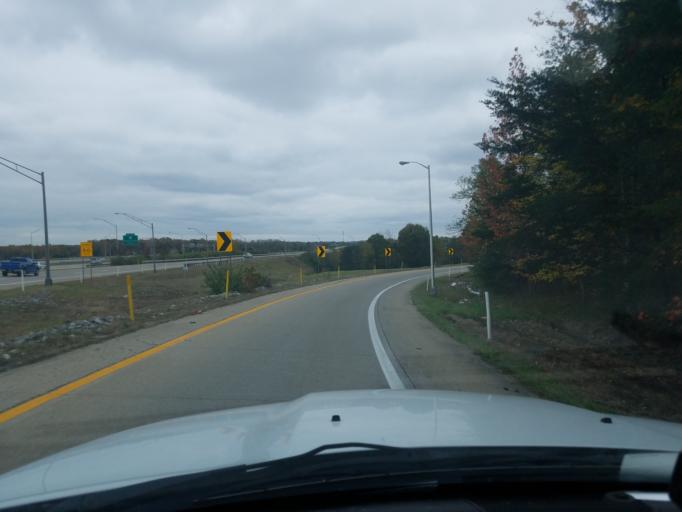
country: US
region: Kentucky
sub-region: Jefferson County
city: Heritage Creek
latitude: 38.1149
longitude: -85.7078
